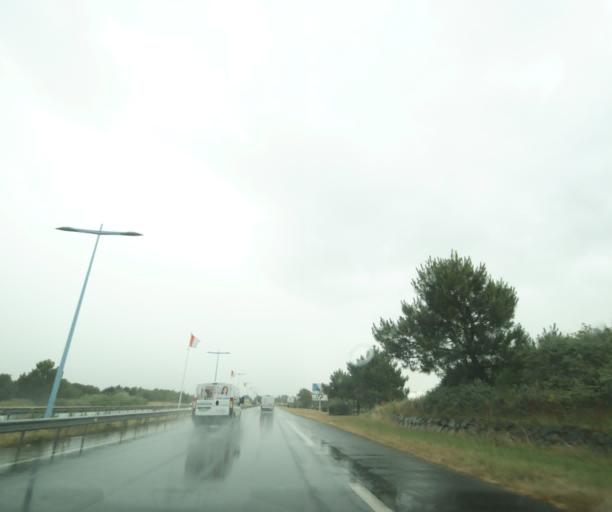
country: FR
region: Pays de la Loire
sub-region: Departement de la Vendee
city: Chateau-d'Olonne
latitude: 46.5170
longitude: -1.7530
